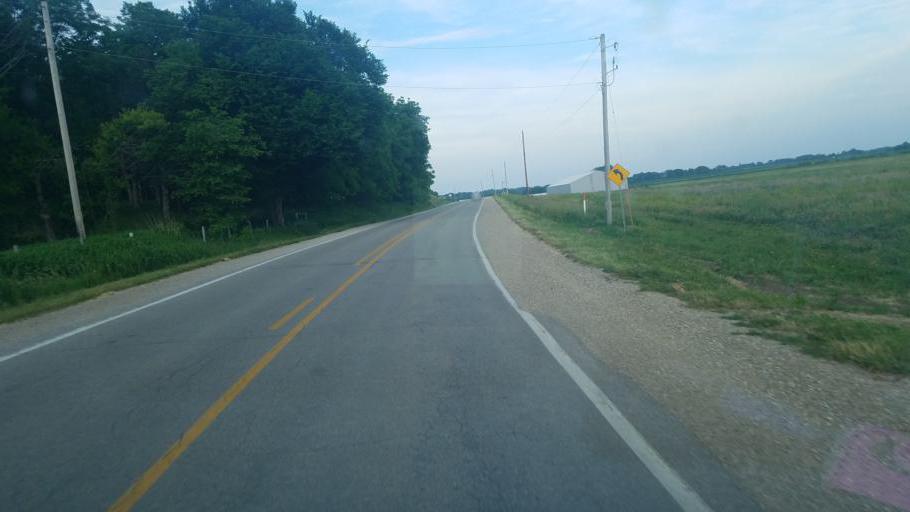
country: US
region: Iowa
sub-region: Benton County
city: Belle Plaine
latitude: 41.9202
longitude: -92.3752
